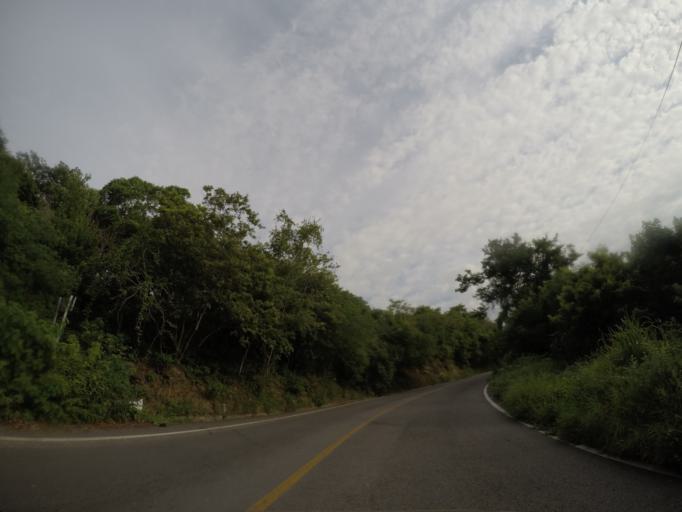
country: MX
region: Oaxaca
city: San Pedro Pochutla
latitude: 15.7062
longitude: -96.4823
